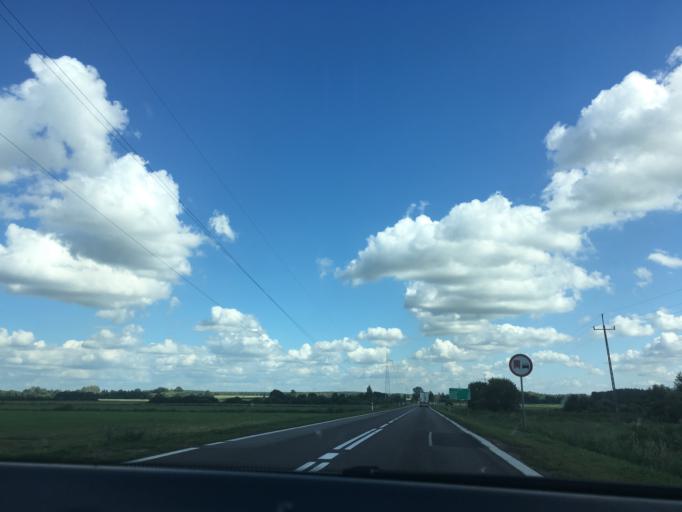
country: PL
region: Podlasie
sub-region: Powiat sokolski
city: Suchowola
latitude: 53.6764
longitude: 23.1064
